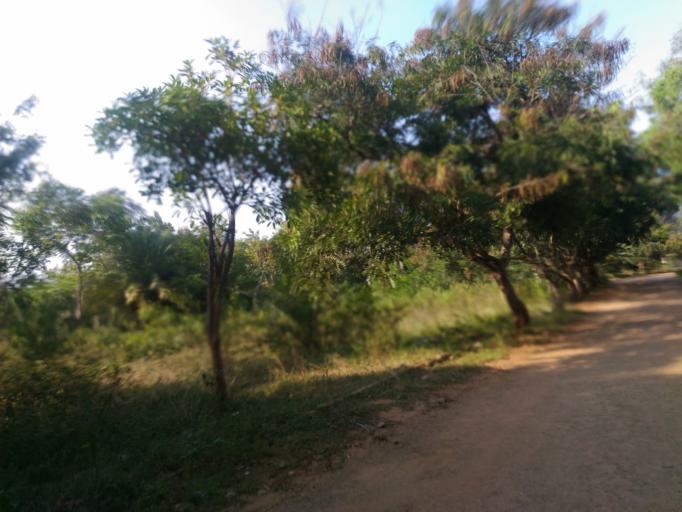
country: IN
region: Karnataka
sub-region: Bangalore Urban
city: Bangalore
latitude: 12.9373
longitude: 77.4995
